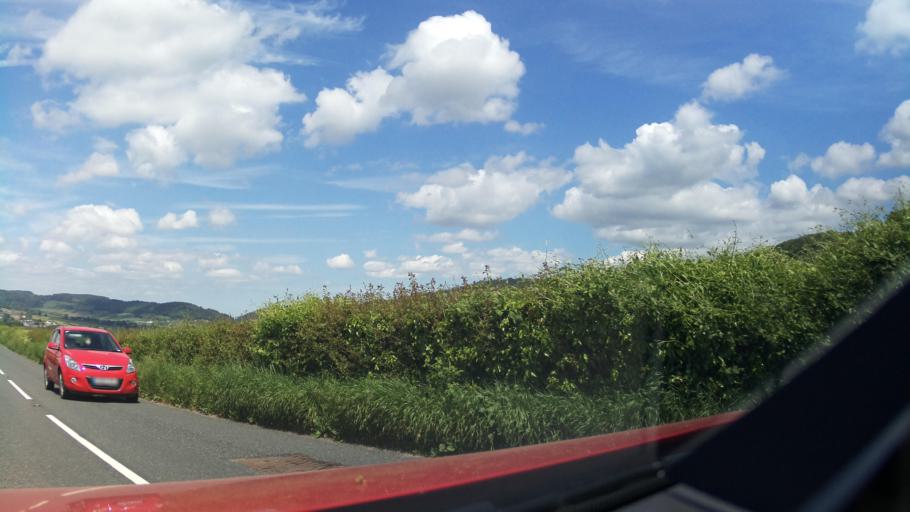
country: GB
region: Wales
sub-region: Monmouthshire
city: Mitchel Troy
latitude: 51.7910
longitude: -2.7161
